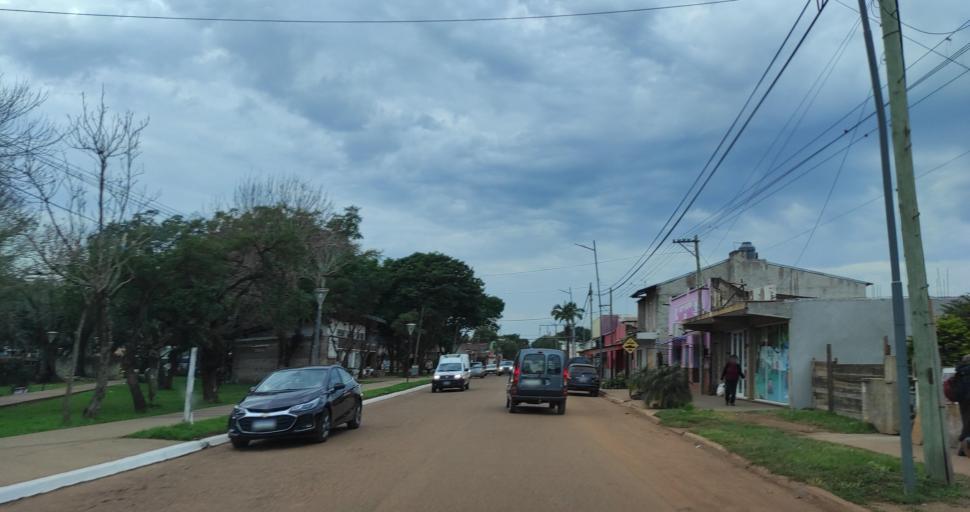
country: AR
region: Corrientes
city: Santo Tome
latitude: -28.5519
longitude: -56.0466
